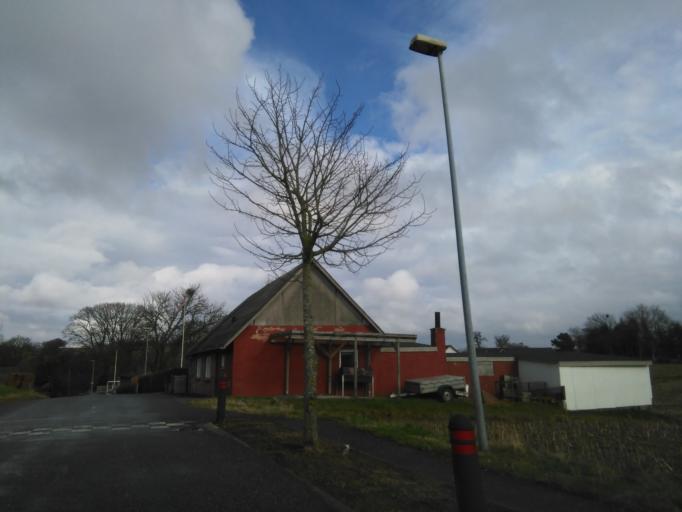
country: DK
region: Central Jutland
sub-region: Skanderborg Kommune
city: Ry
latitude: 56.1108
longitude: 9.8155
